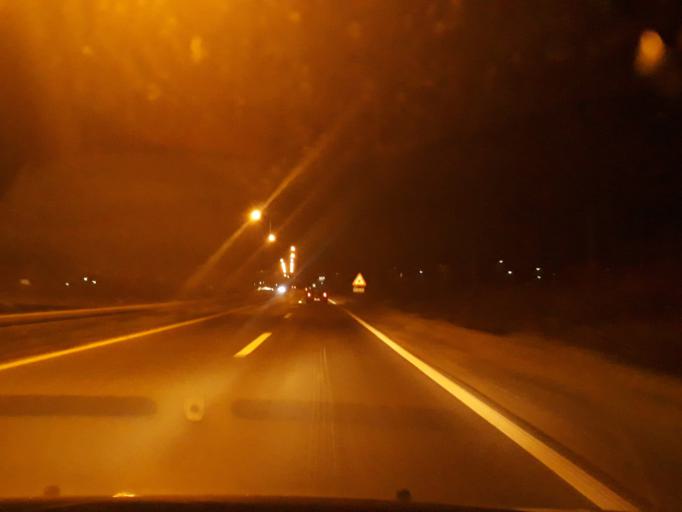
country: BA
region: Federation of Bosnia and Herzegovina
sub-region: Kanton Sarajevo
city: Sarajevo
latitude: 43.8331
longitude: 18.2832
